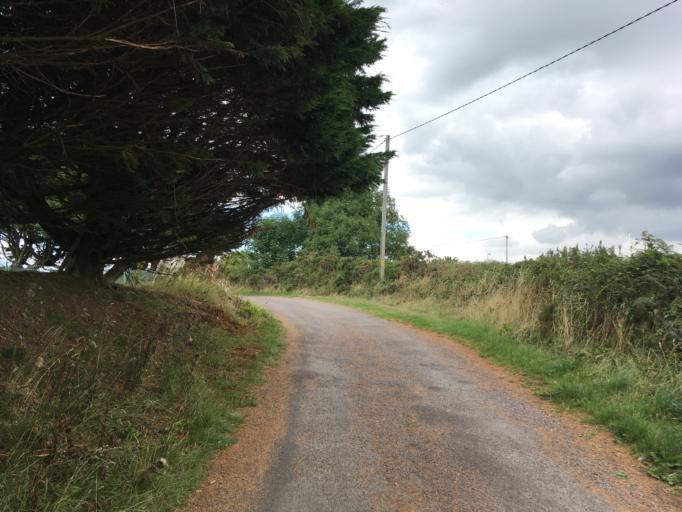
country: IE
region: Munster
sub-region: County Cork
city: Crosshaven
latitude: 51.8077
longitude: -8.2802
